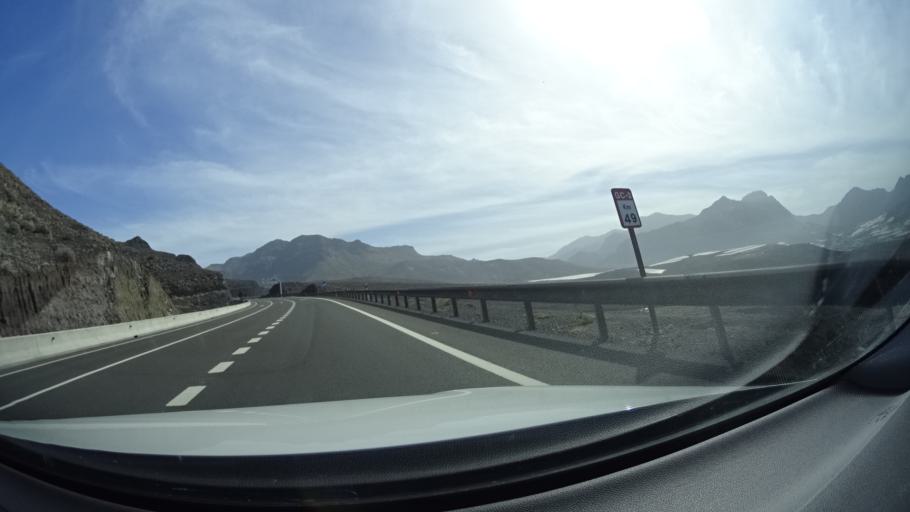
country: ES
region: Canary Islands
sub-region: Provincia de Las Palmas
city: San Nicolas
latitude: 28.0079
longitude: -15.7937
